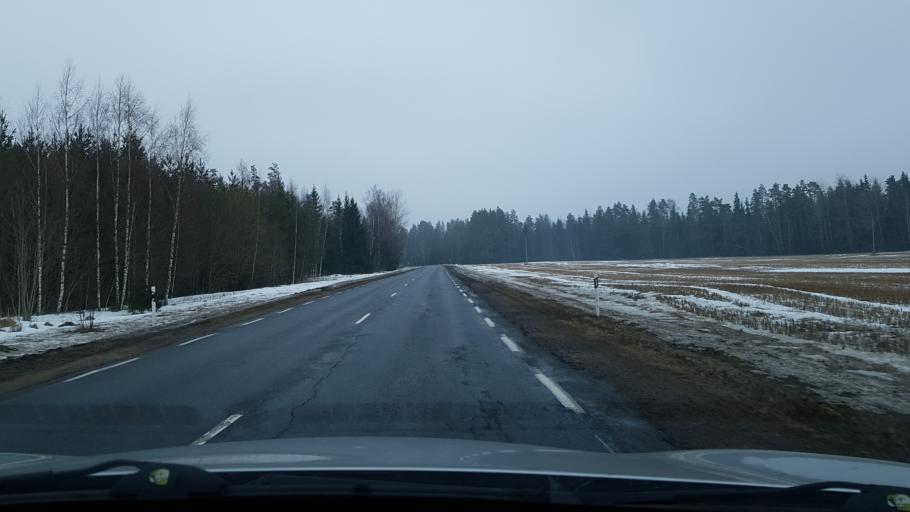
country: EE
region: Valgamaa
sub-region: Torva linn
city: Torva
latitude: 58.1658
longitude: 25.9629
